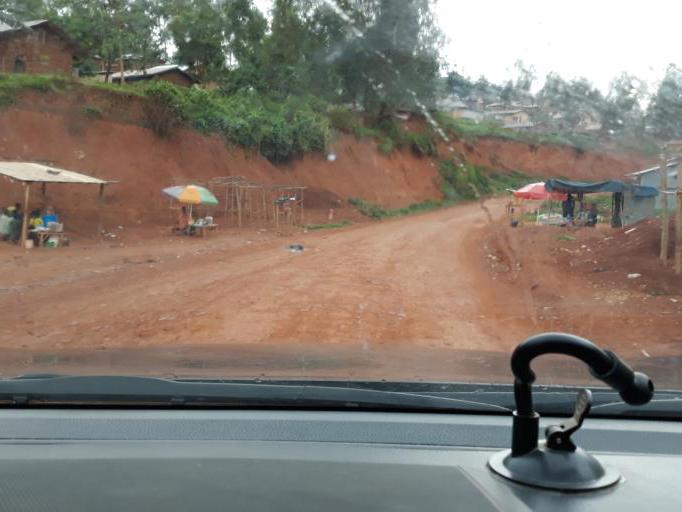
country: CD
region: Eastern Province
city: Bunia
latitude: 1.7282
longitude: 30.3078
